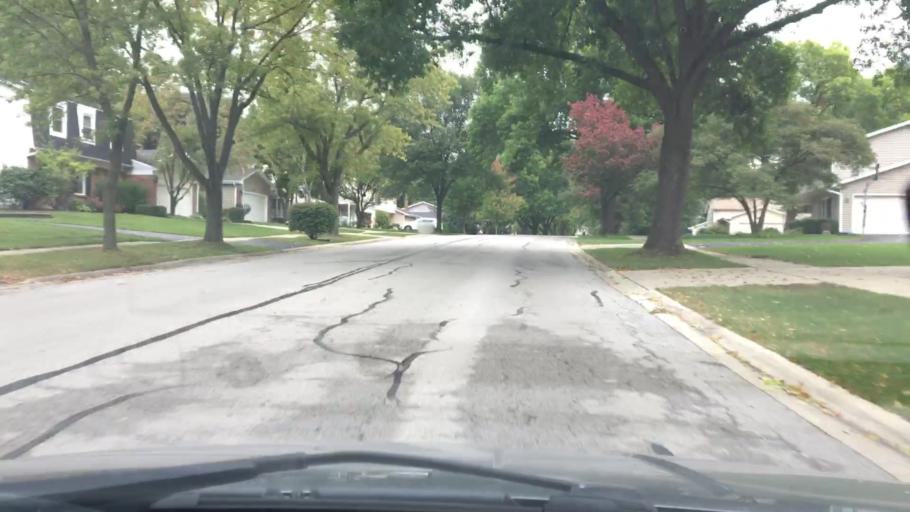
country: US
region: Illinois
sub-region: DuPage County
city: Naperville
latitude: 41.7432
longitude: -88.1355
